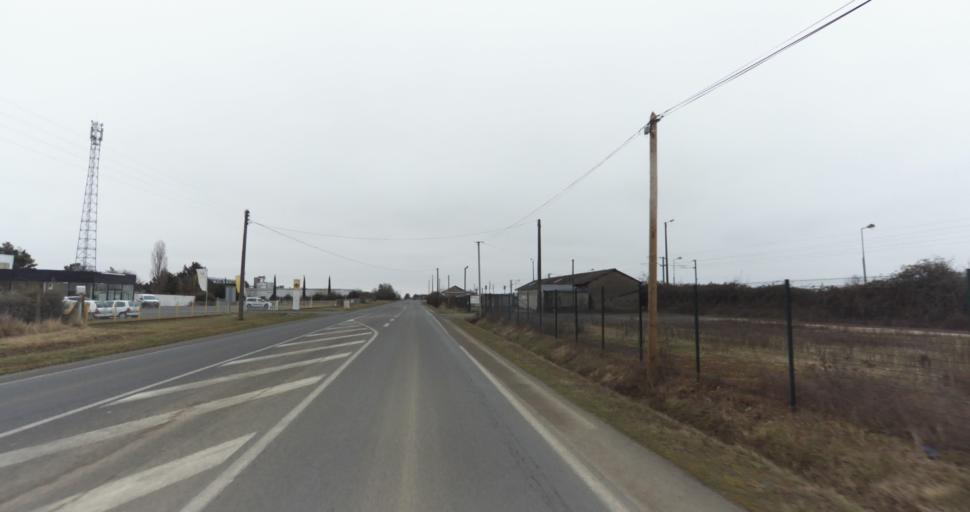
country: FR
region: Pays de la Loire
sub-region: Departement de Maine-et-Loire
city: Montreuil-Bellay
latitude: 47.1231
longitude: -0.1414
